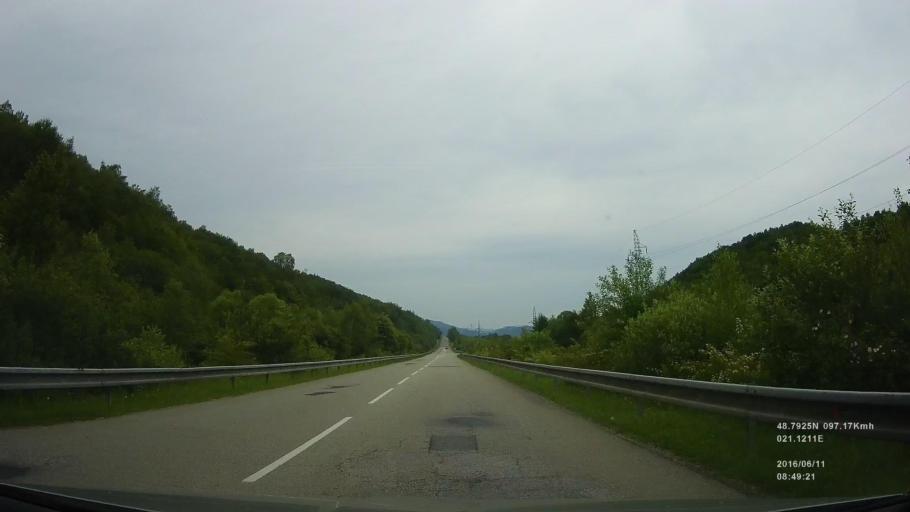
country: SK
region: Kosicky
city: Kosice
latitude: 48.7861
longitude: 21.1255
